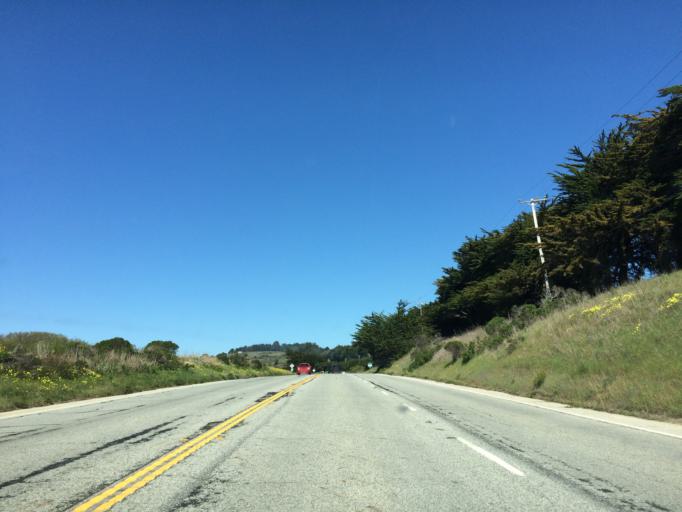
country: US
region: California
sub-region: Santa Cruz County
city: Boulder Creek
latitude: 37.1692
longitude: -122.3620
